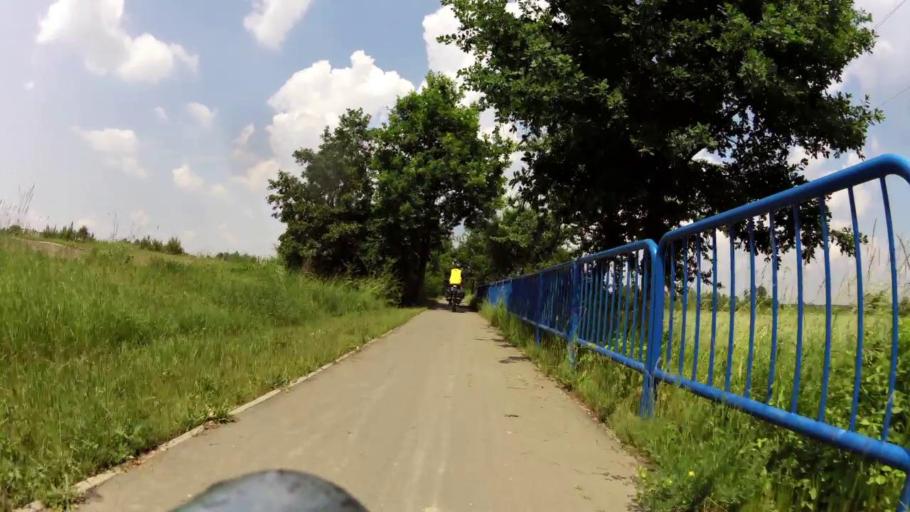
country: PL
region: Kujawsko-Pomorskie
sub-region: Powiat bydgoski
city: Koronowo
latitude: 53.2878
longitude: 17.9470
